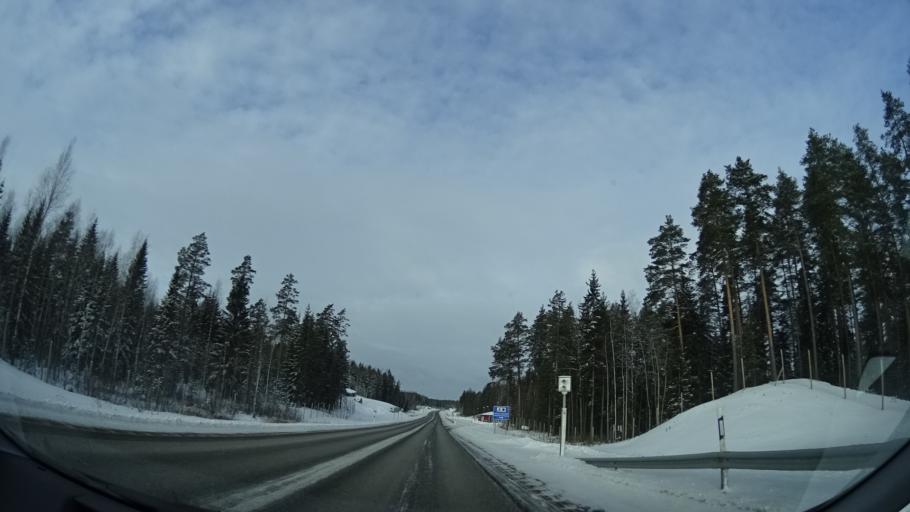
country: FI
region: Uusimaa
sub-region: Helsinki
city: Karkkila
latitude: 60.5904
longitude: 24.1106
